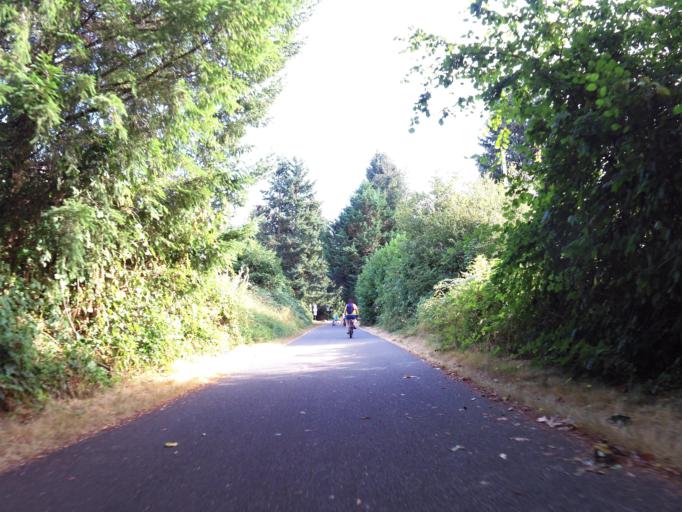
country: US
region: Washington
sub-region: Thurston County
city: Lacey
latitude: 47.0286
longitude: -122.8369
